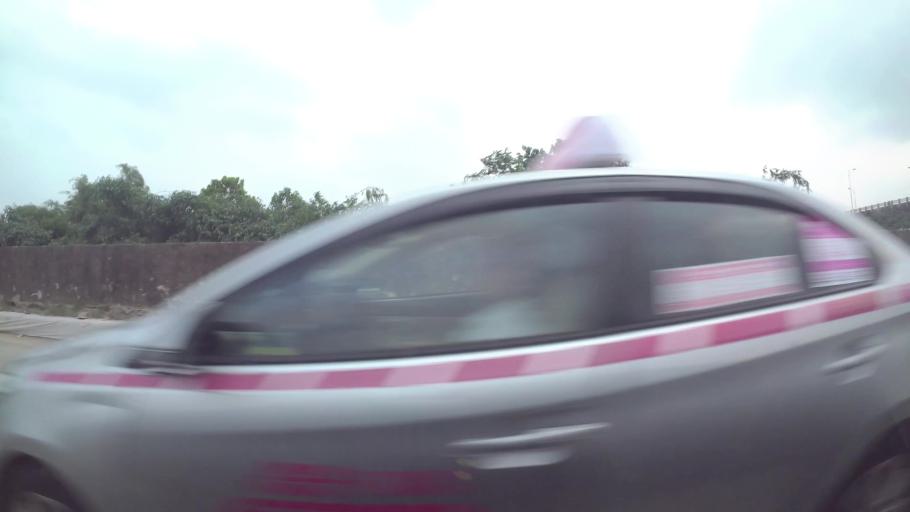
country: VN
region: Ha Noi
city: Trau Quy
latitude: 21.0217
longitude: 105.8937
